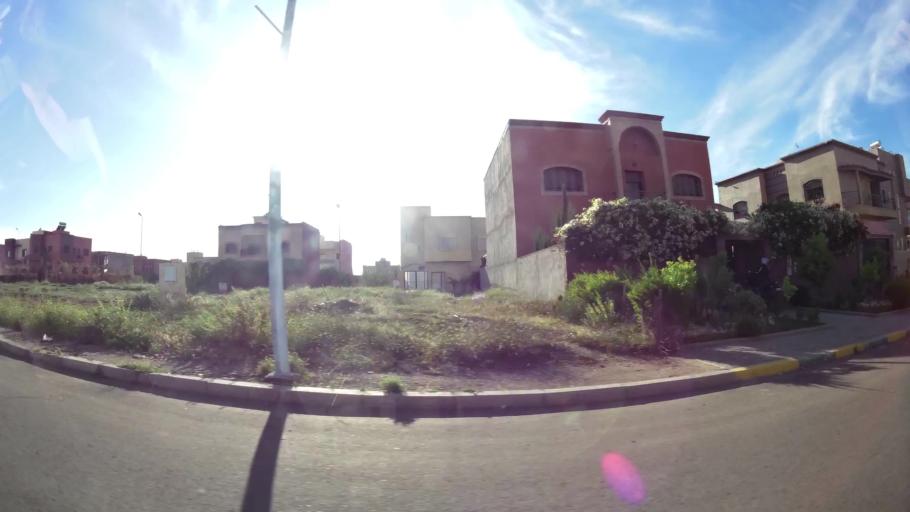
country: MA
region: Marrakech-Tensift-Al Haouz
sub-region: Marrakech
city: Marrakesh
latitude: 31.6802
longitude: -8.0625
